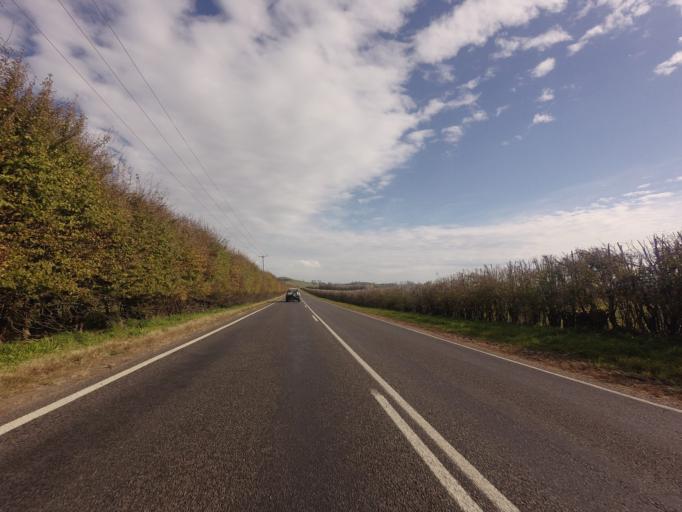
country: AU
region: Tasmania
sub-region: Meander Valley
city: Westbury
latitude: -41.5242
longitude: 146.7717
